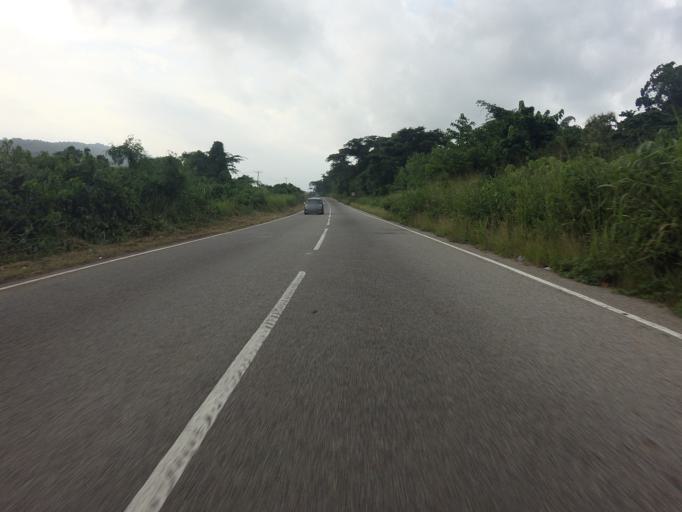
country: GH
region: Volta
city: Ho
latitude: 6.6434
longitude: 0.4689
